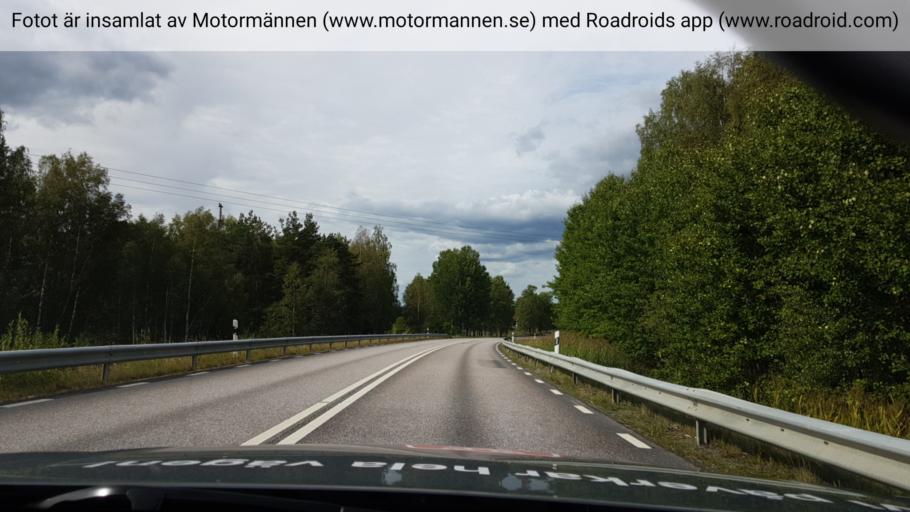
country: SE
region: Uppsala
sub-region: Heby Kommun
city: Morgongava
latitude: 59.9175
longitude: 17.0067
